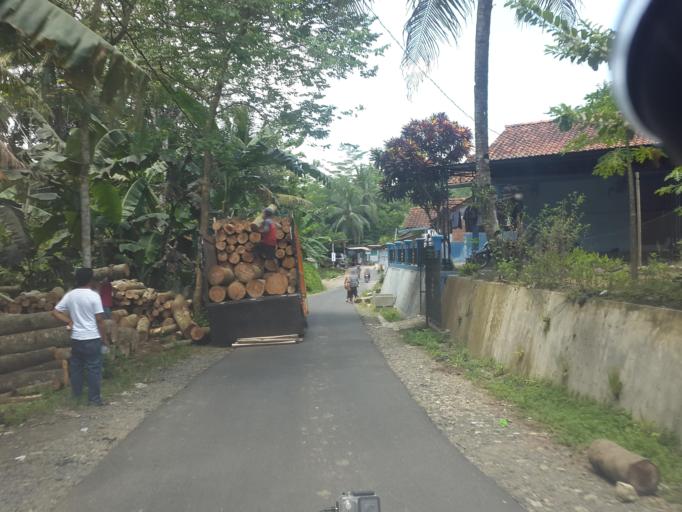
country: ID
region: Central Java
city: Sangkalputung
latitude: -7.4187
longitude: 109.0442
